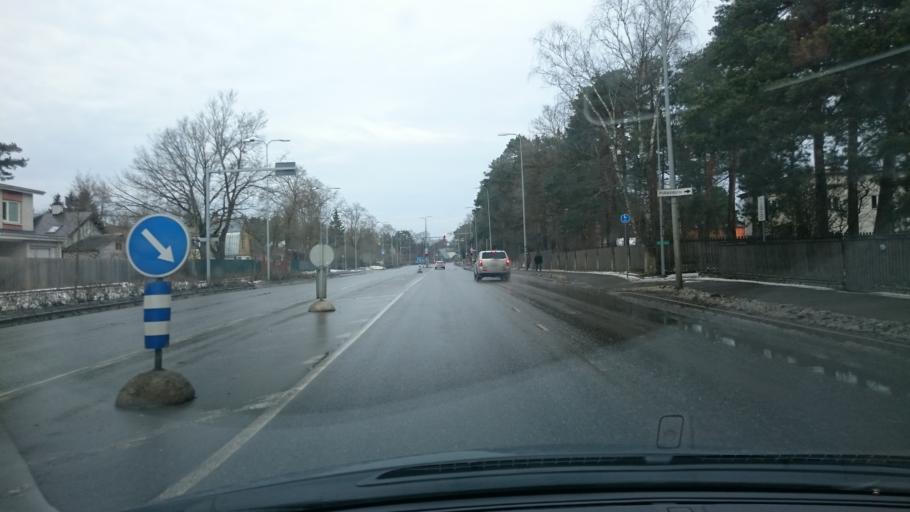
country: EE
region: Harju
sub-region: Tallinna linn
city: Tallinn
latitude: 59.3836
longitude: 24.7176
